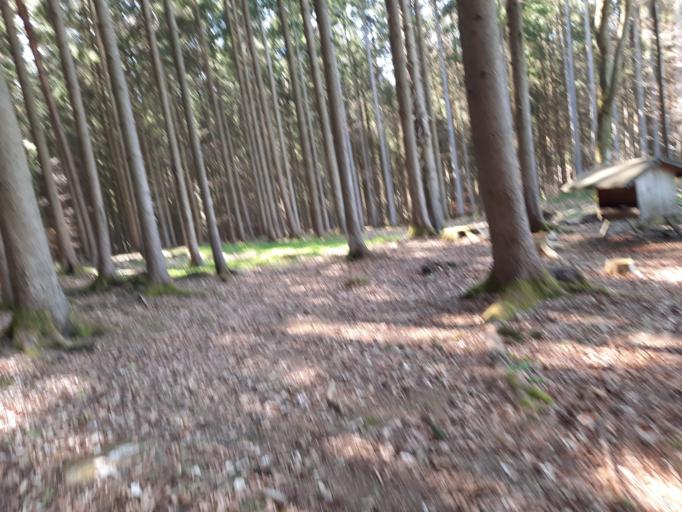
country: DE
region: Bavaria
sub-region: Upper Bavaria
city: Moosach
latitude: 48.0436
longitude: 11.8920
